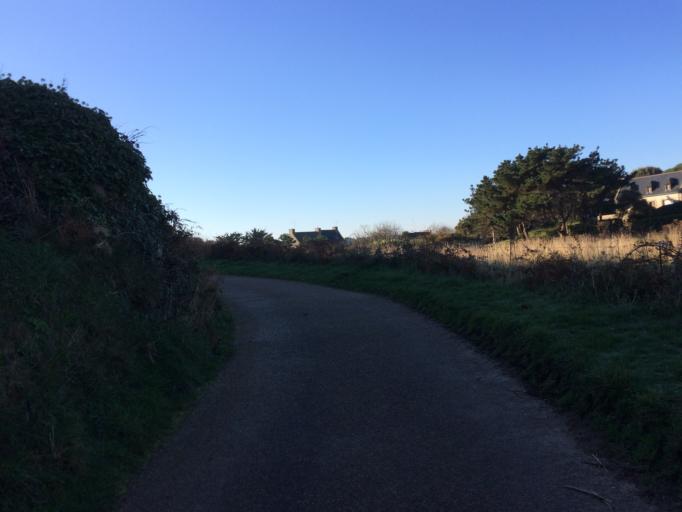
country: FR
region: Brittany
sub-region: Departement des Cotes-d'Armor
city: Ploubazlanec
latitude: 48.8611
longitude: -2.9941
